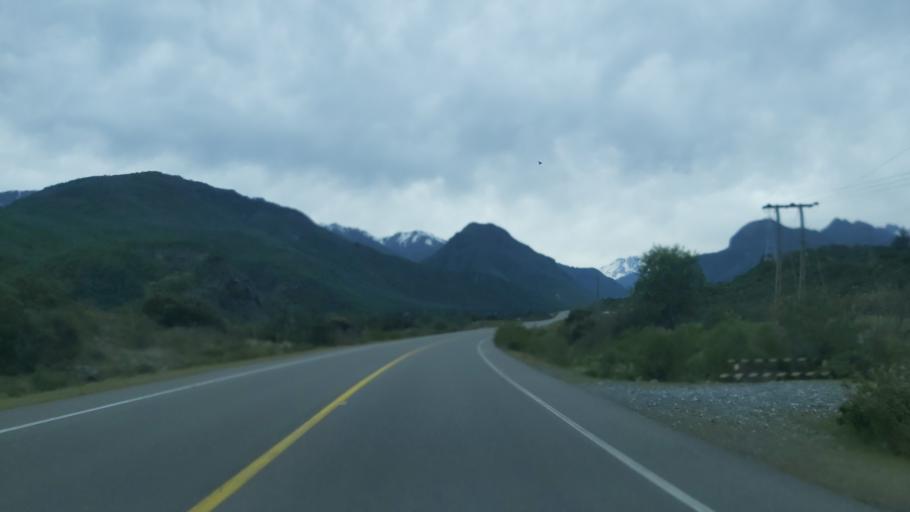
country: CL
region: Maule
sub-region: Provincia de Linares
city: Colbun
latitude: -35.7106
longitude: -71.1091
